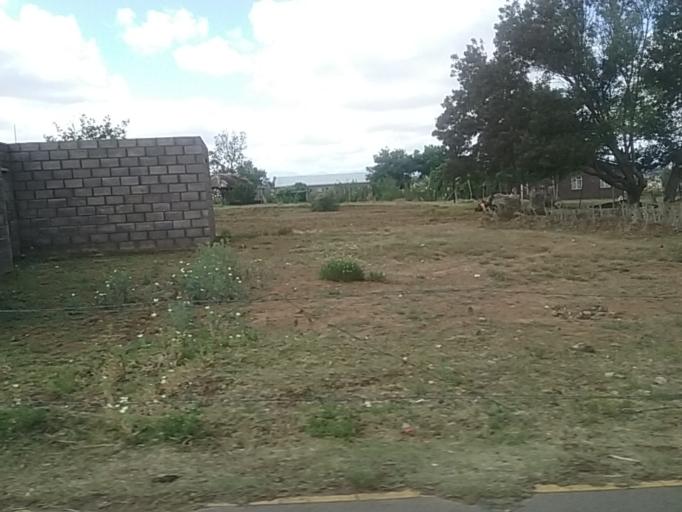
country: LS
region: Berea
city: Teyateyaneng
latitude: -29.1369
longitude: 27.7326
